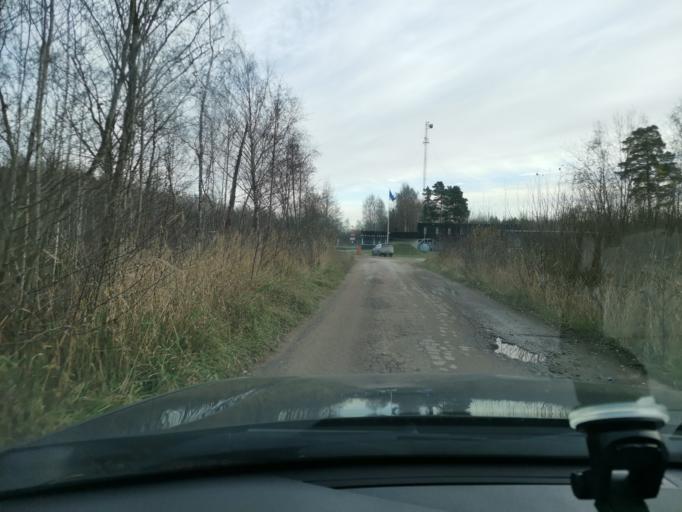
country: EE
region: Ida-Virumaa
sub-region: Sillamaee linn
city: Sillamae
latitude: 59.2583
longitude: 27.9142
